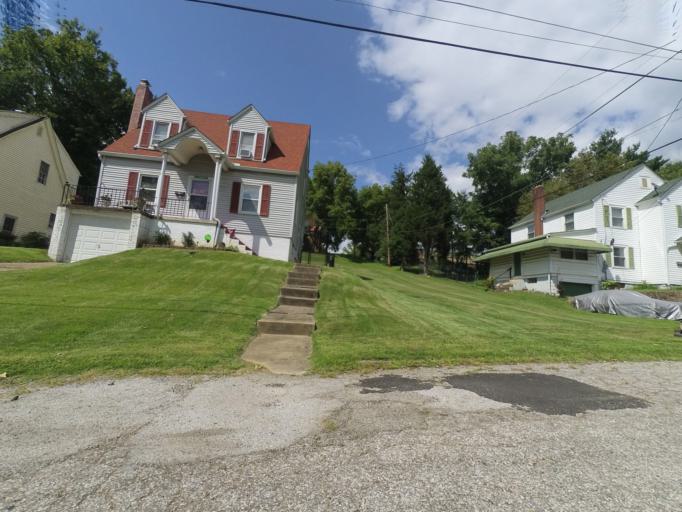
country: US
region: West Virginia
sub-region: Cabell County
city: Huntington
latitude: 38.4067
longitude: -82.4242
